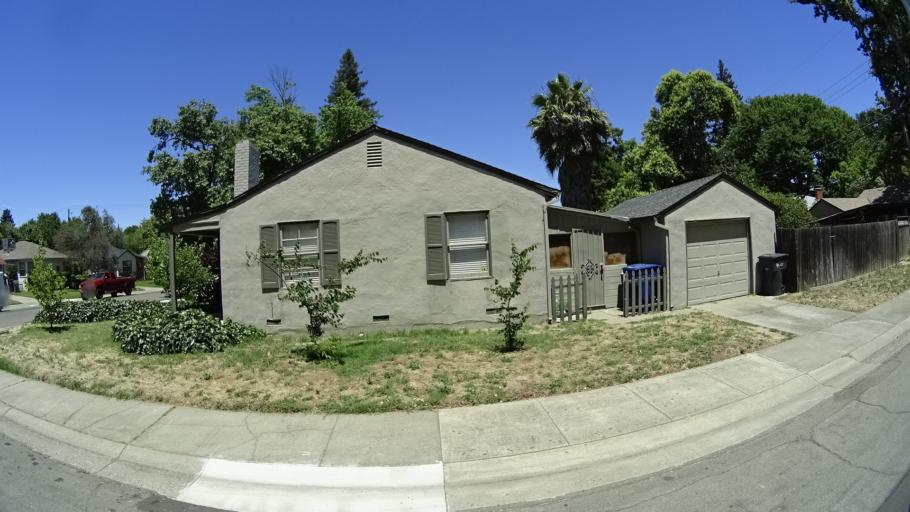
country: US
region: California
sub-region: Sacramento County
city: Sacramento
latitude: 38.5774
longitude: -121.4403
